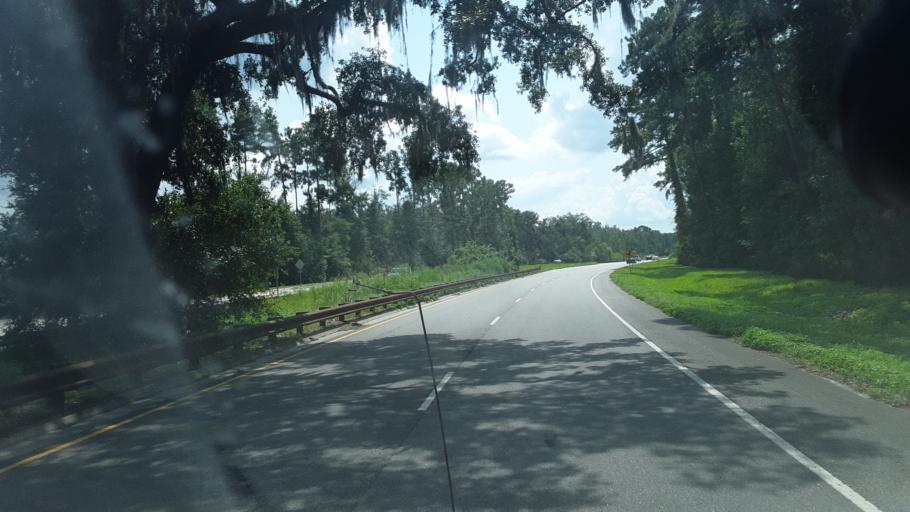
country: US
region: South Carolina
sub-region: Beaufort County
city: Bluffton
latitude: 32.2762
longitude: -80.9472
